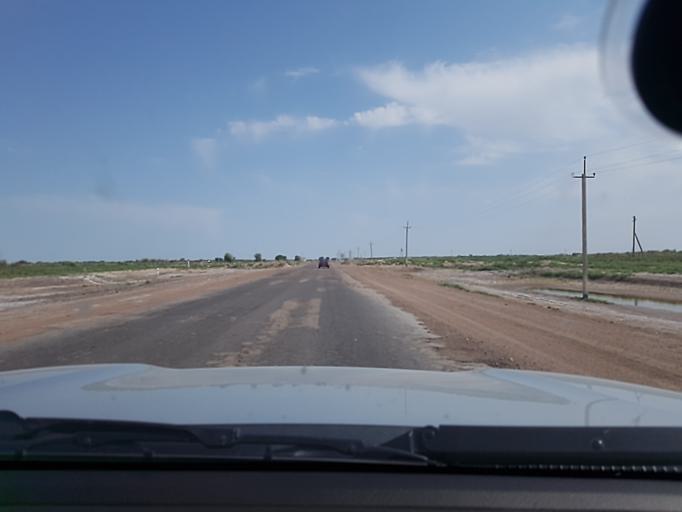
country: TM
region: Dasoguz
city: Boldumsaz
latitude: 42.1759
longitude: 59.5776
